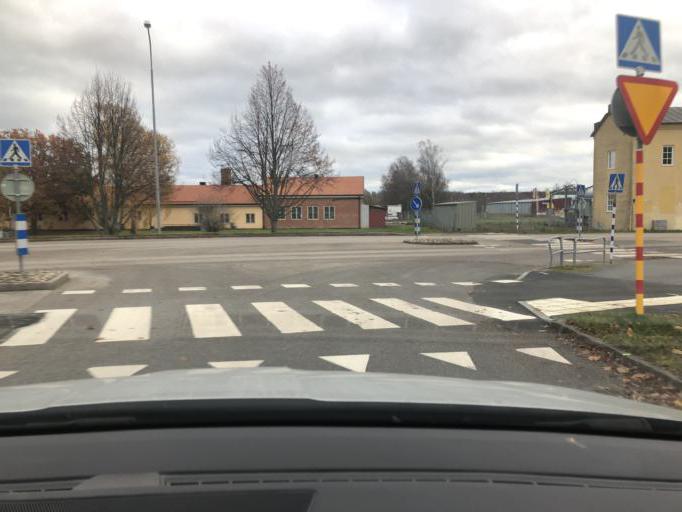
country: SE
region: Uppsala
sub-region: Tierps Kommun
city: Tierp
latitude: 60.3439
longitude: 17.5214
